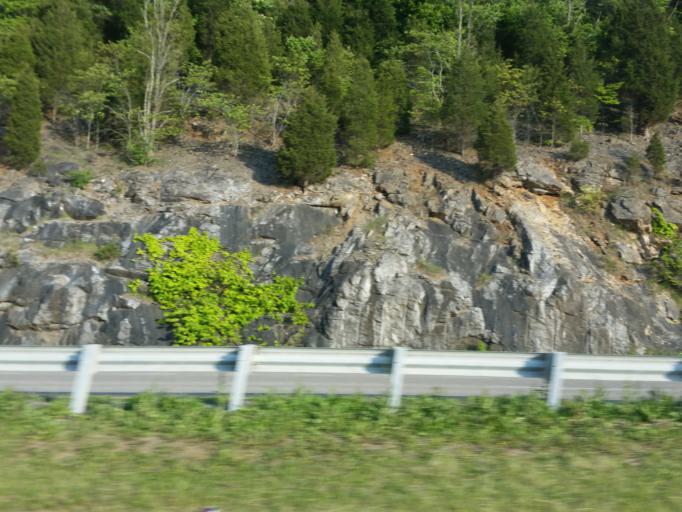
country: US
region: Virginia
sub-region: Russell County
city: Lebanon
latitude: 36.8873
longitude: -82.1021
